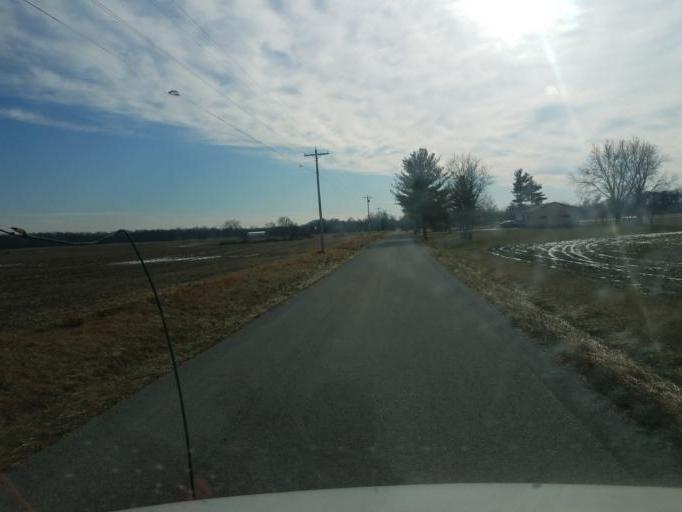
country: US
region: Ohio
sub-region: Delaware County
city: Ashley
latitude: 40.3908
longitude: -82.9364
